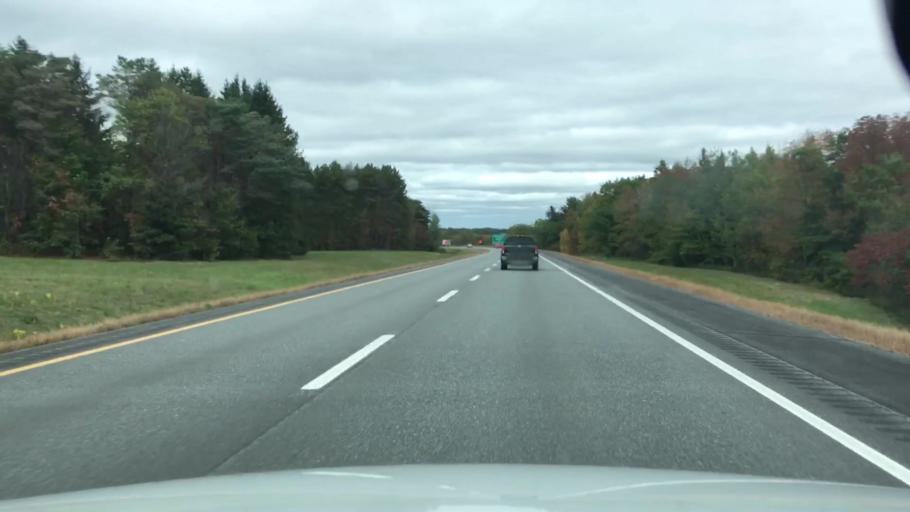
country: US
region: Maine
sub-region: Somerset County
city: Pittsfield
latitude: 44.7648
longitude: -69.4124
